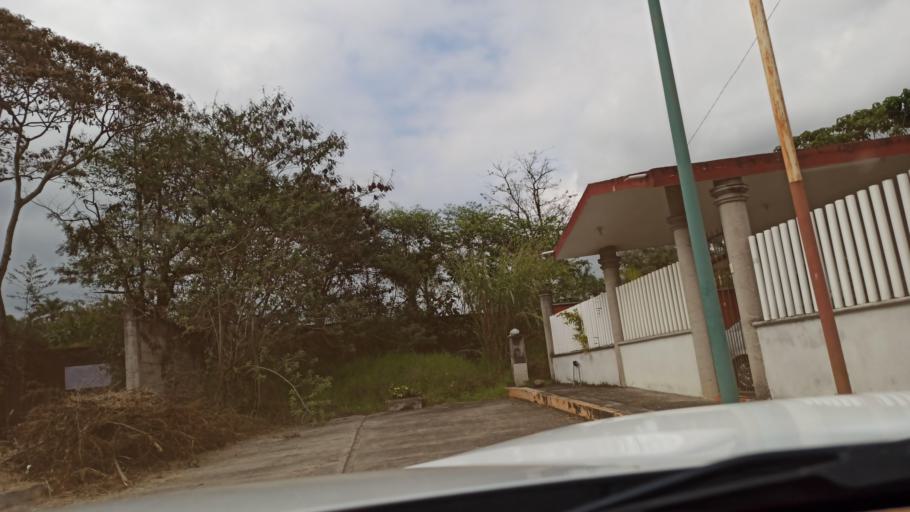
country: MX
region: Veracruz
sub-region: Fortin
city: Fortin de las Flores
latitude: 18.9029
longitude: -96.9940
